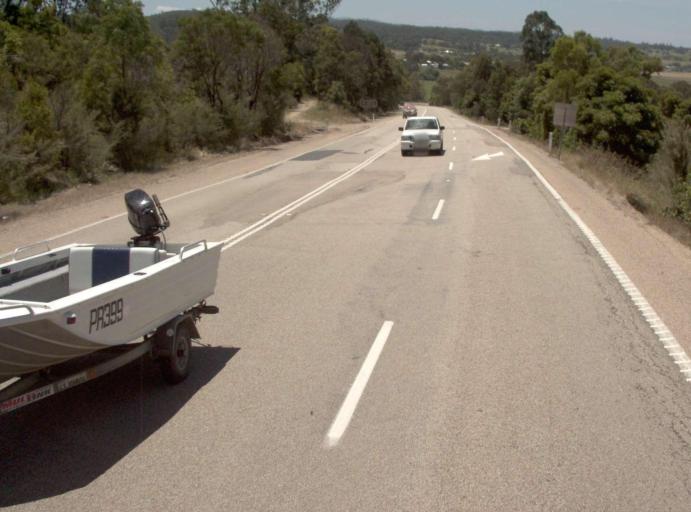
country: AU
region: Victoria
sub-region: East Gippsland
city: Bairnsdale
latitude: -37.7238
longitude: 147.8025
